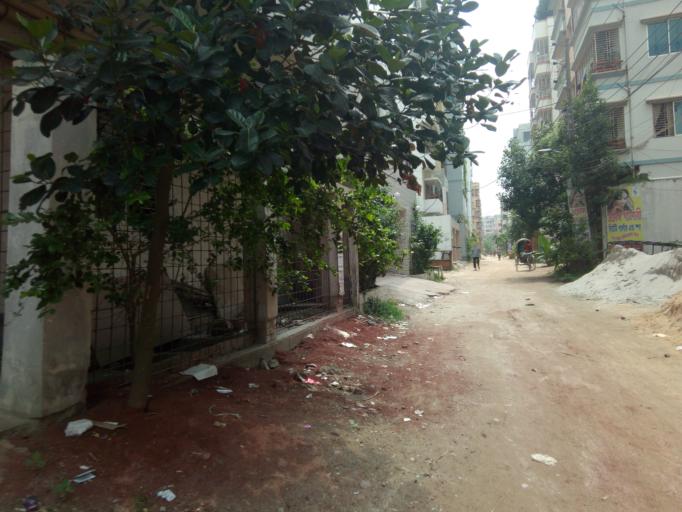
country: BD
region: Dhaka
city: Paltan
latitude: 23.7588
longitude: 90.4439
